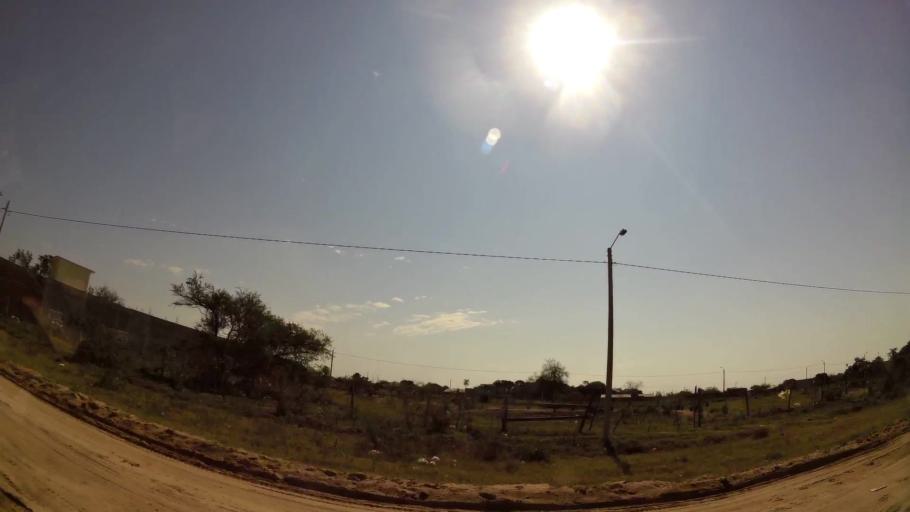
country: BO
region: Santa Cruz
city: Cotoca
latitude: -17.7247
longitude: -63.0695
